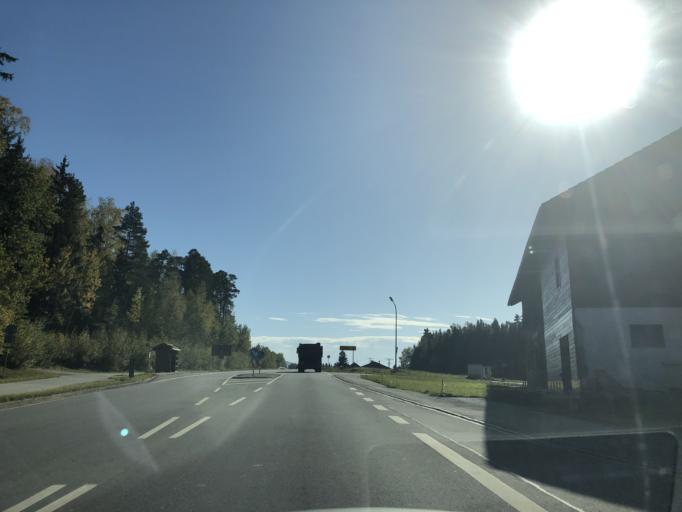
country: DE
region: Bavaria
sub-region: Lower Bavaria
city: Patersdorf
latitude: 49.0107
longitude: 12.9828
